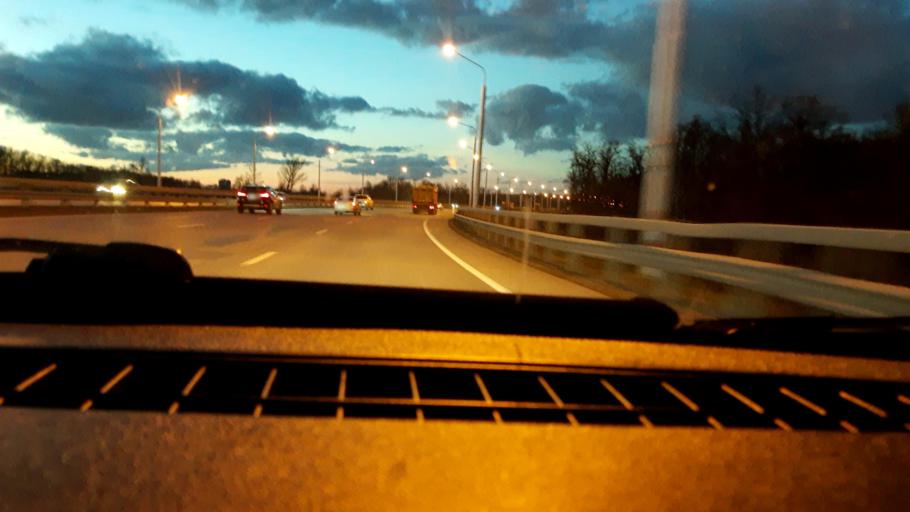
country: RU
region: Bashkortostan
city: Mikhaylovka
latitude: 54.7823
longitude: 55.9148
